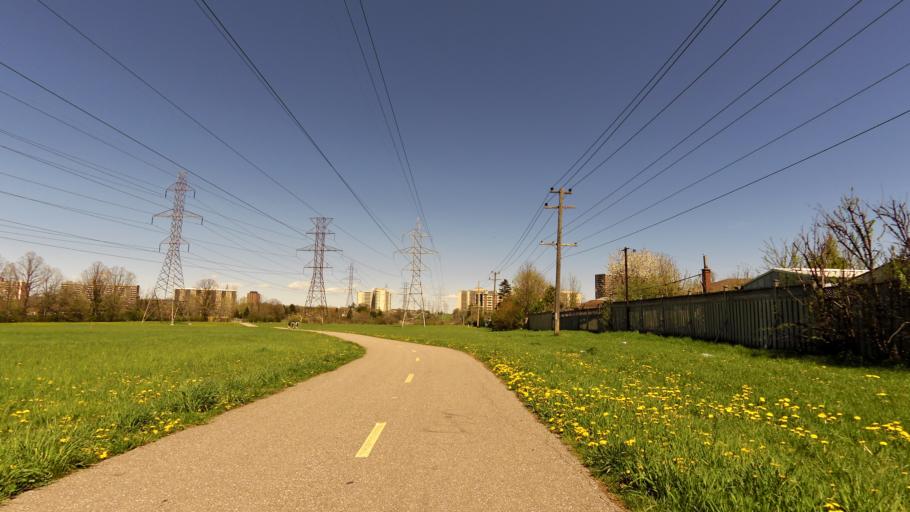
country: CA
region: Ontario
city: Concord
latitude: 43.7606
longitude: -79.5158
